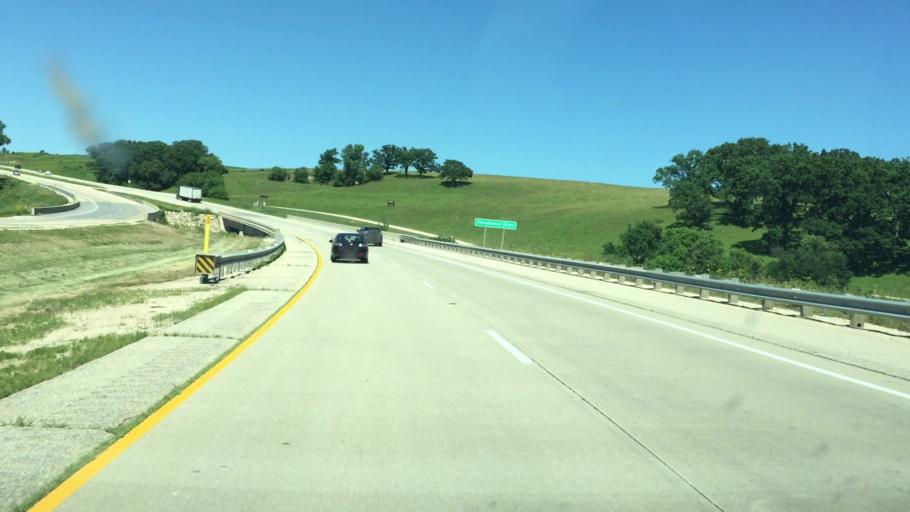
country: US
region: Wisconsin
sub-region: Iowa County
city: Mineral Point
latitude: 42.8110
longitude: -90.2591
